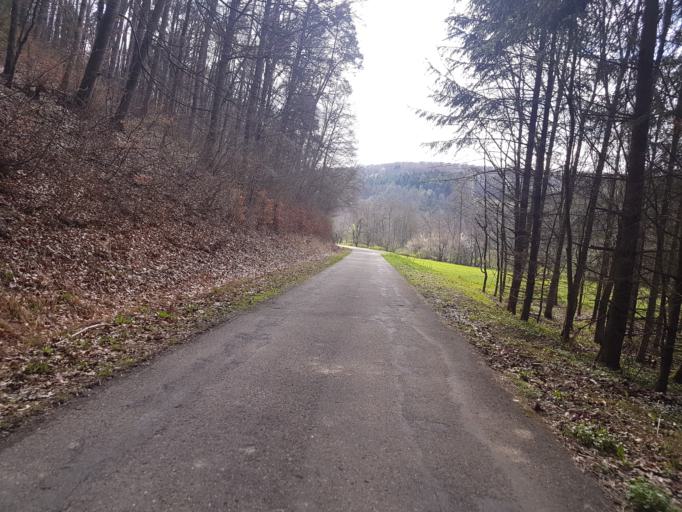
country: DE
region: Baden-Wuerttemberg
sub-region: Regierungsbezirk Stuttgart
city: Krautheim
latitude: 49.3542
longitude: 9.6129
